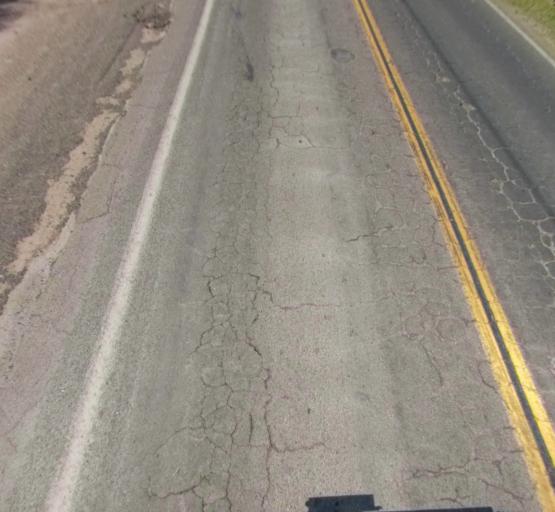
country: US
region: California
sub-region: Madera County
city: Chowchilla
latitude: 37.0979
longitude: -120.2567
